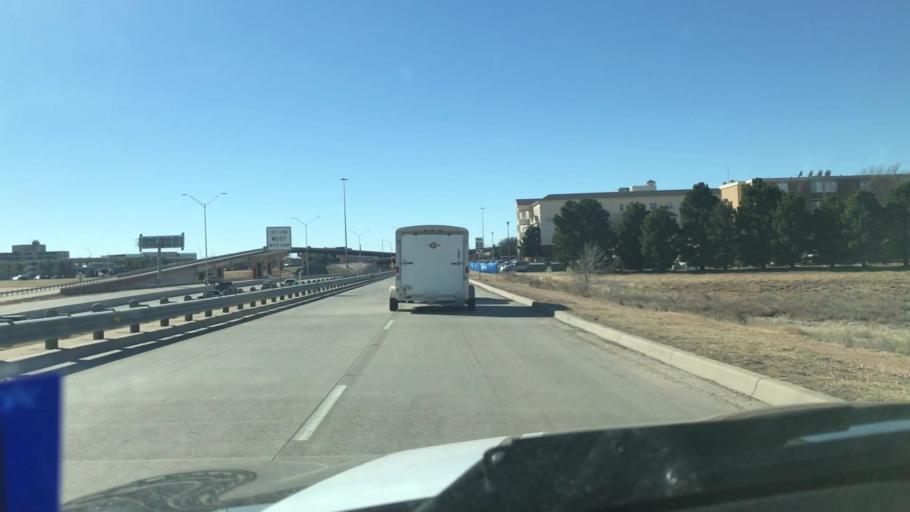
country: US
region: Texas
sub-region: Lubbock County
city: Lubbock
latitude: 33.5811
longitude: -101.8955
